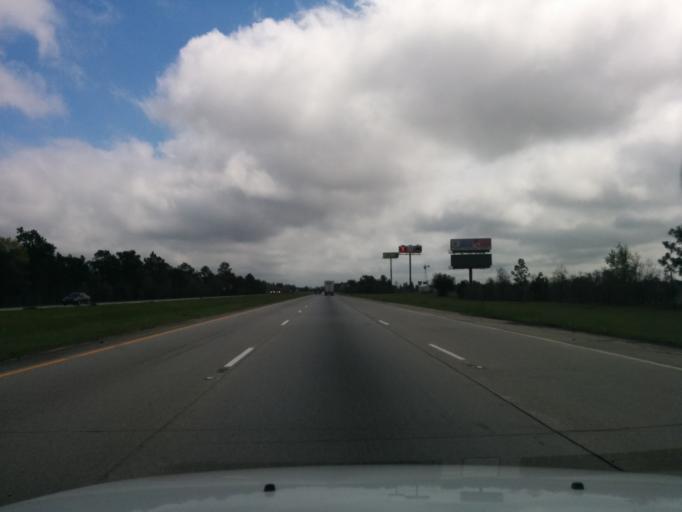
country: US
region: Georgia
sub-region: Toombs County
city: Lyons
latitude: 32.3976
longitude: -82.3022
